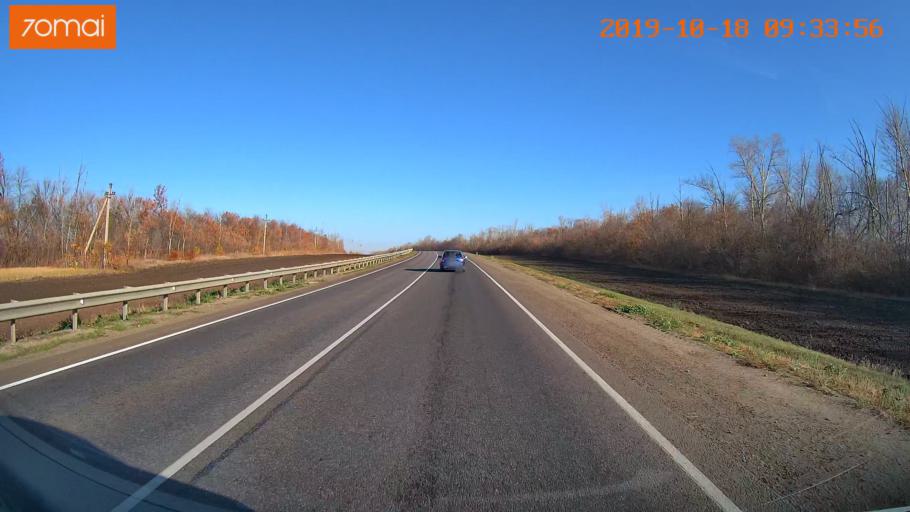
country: RU
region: Tula
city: Yefremov
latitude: 53.1736
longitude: 38.1526
